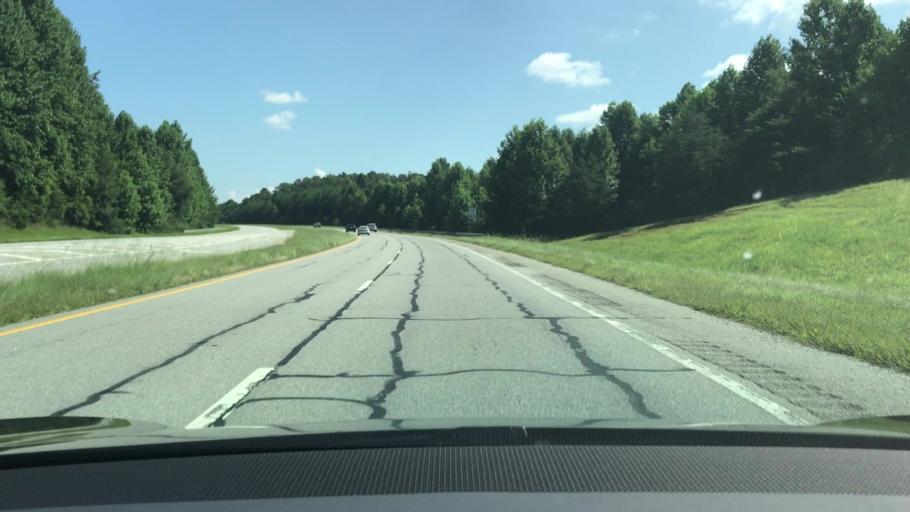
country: US
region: Georgia
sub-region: Habersham County
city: Clarkesville
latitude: 34.6600
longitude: -83.4349
